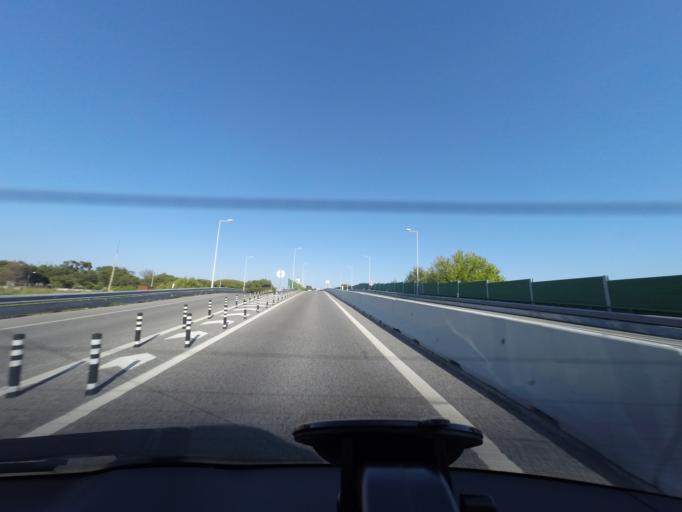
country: PT
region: Lisbon
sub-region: Cascais
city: Cascais
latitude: 38.7220
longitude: -9.4451
